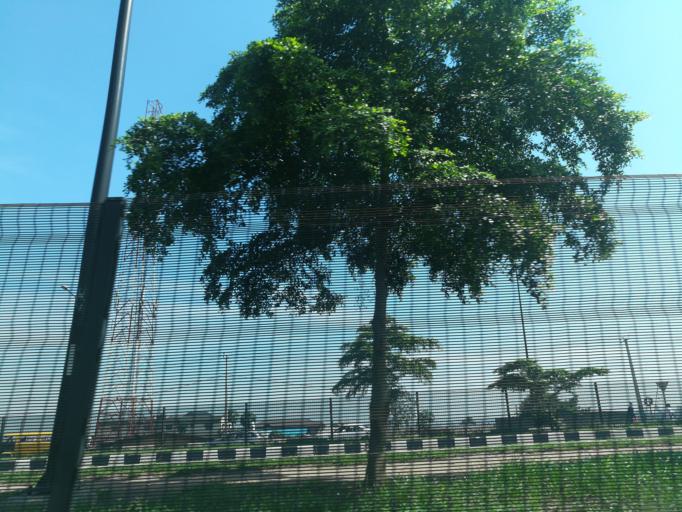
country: NG
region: Lagos
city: Ebute Ikorodu
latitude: 6.6195
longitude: 3.4734
